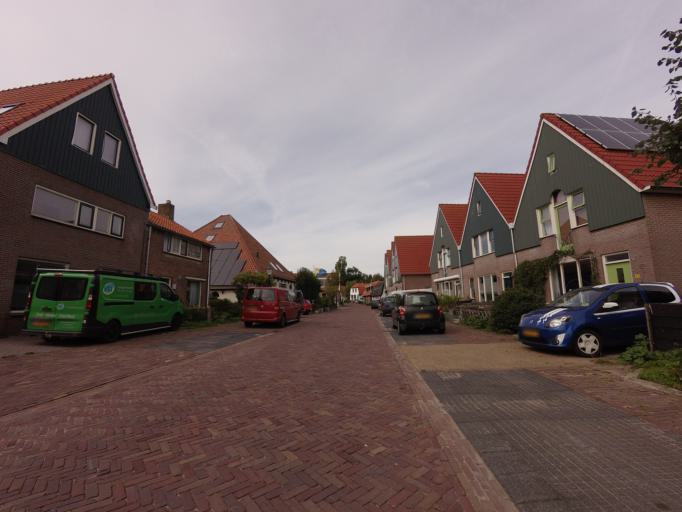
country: NL
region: North Holland
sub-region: Gemeente Texel
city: Den Burg
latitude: 53.0721
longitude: 4.8248
